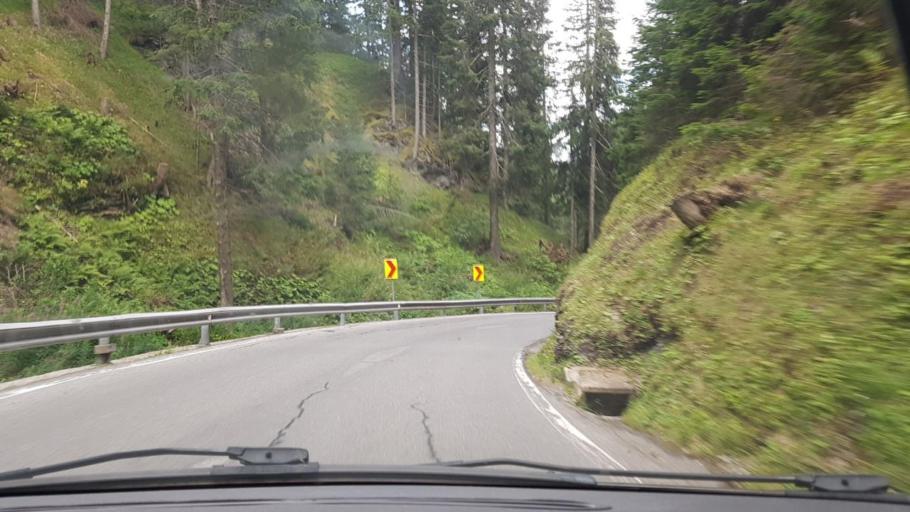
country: AT
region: Salzburg
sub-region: Politischer Bezirk Tamsweg
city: Sankt Michael im Lungau
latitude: 47.0495
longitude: 13.6166
